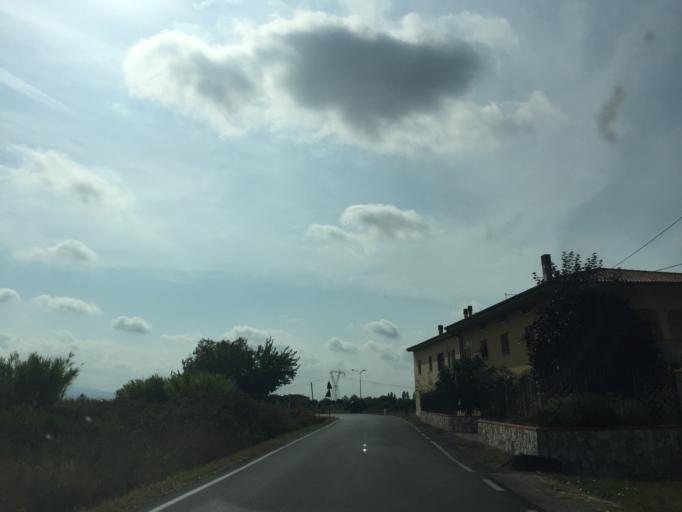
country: IT
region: Tuscany
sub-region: Provincia di Pistoia
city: Cintolese
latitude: 43.8454
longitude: 10.8138
